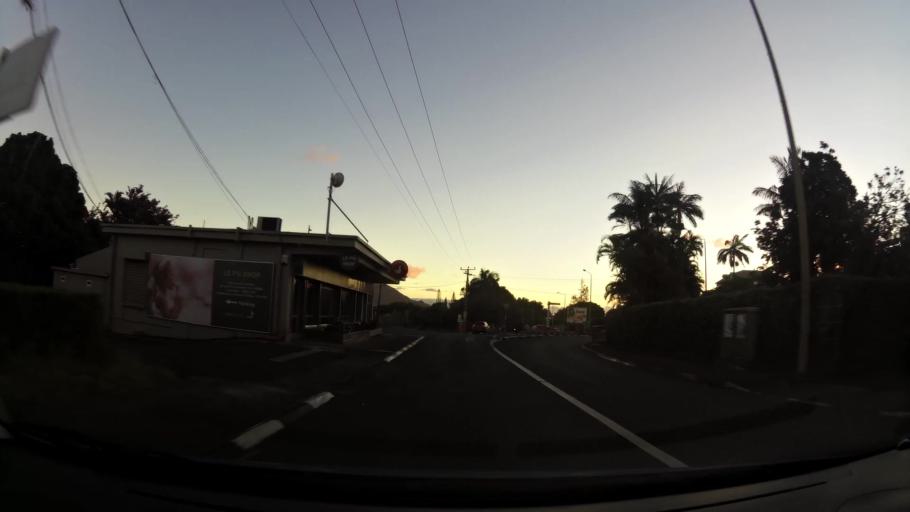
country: MU
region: Moka
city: Moka
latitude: -20.2261
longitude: 57.5074
